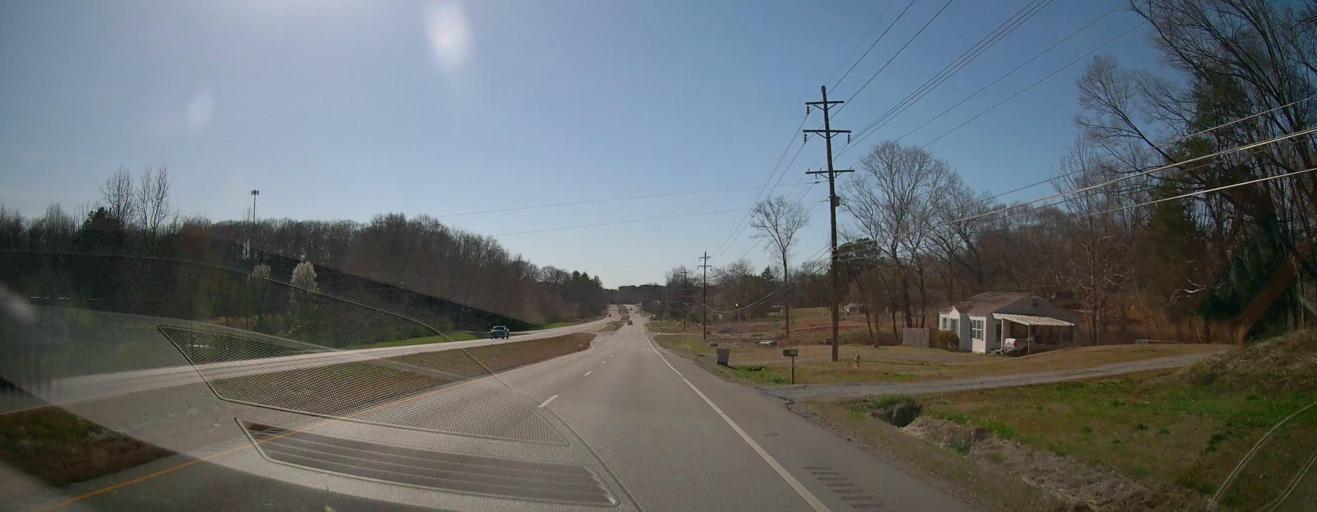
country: US
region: Alabama
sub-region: Lauderdale County
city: Killen
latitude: 34.8597
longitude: -87.5136
